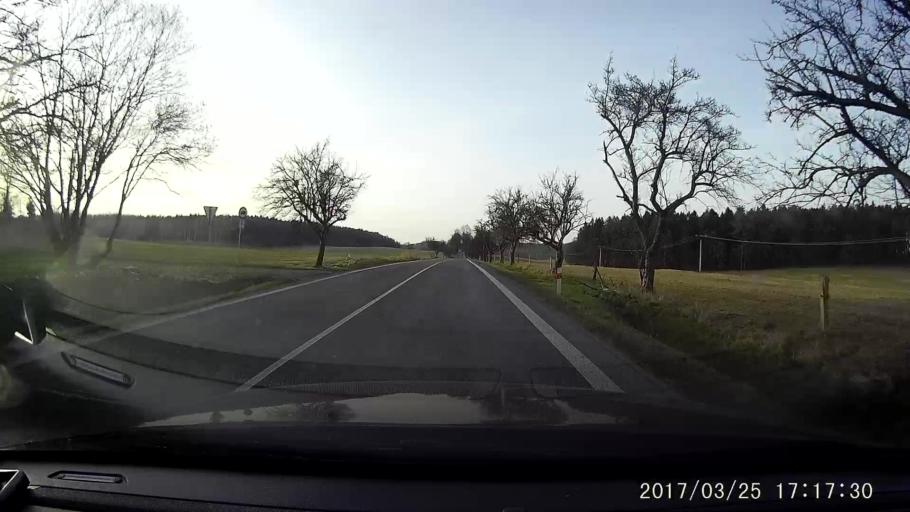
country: CZ
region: Liberecky
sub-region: Okres Liberec
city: Frydlant
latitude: 50.9673
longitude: 15.0963
